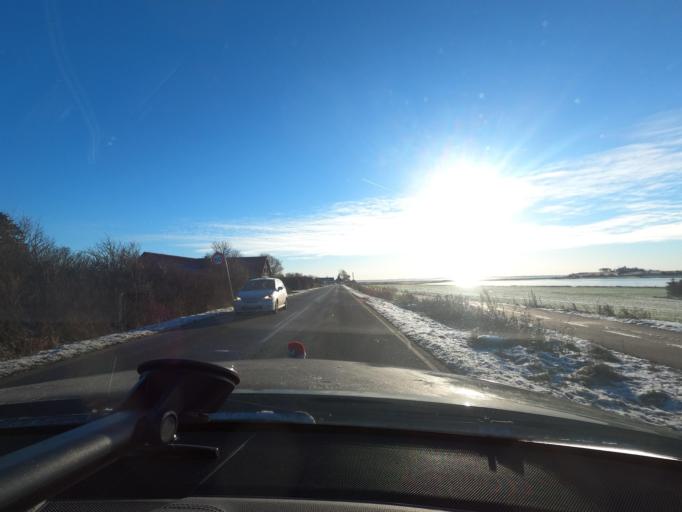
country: DE
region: Schleswig-Holstein
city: Pommerby
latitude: 54.8634
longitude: 9.9979
